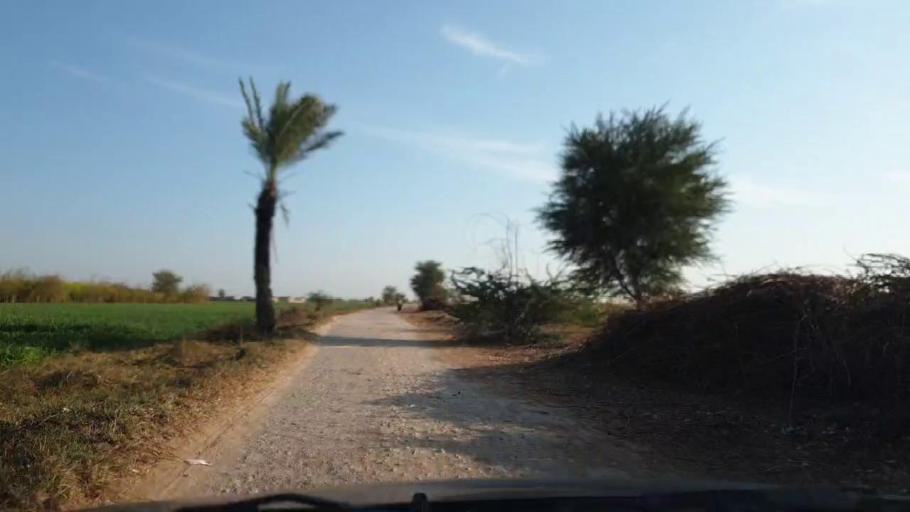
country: PK
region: Sindh
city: Khadro
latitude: 26.2111
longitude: 68.7443
